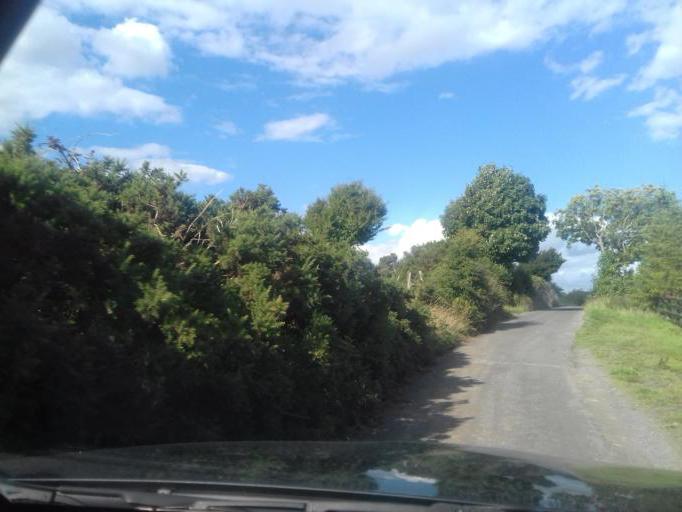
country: IE
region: Leinster
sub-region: Kilkenny
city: Graiguenamanagh
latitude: 52.5527
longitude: -7.0210
